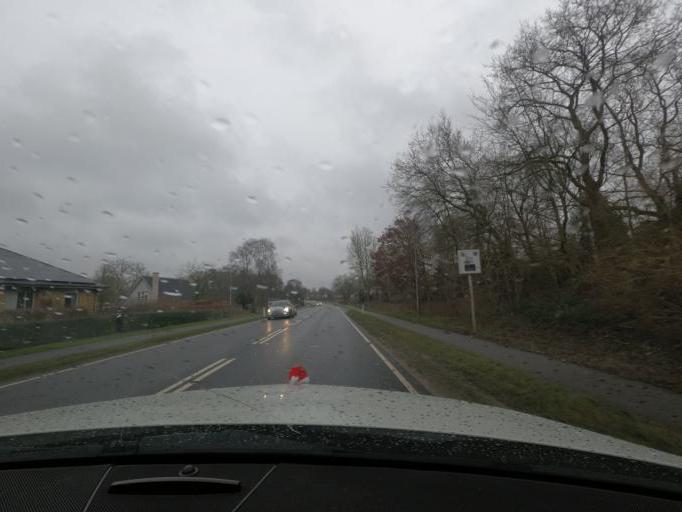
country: DK
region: South Denmark
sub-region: Haderslev Kommune
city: Starup
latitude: 55.2432
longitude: 9.5278
